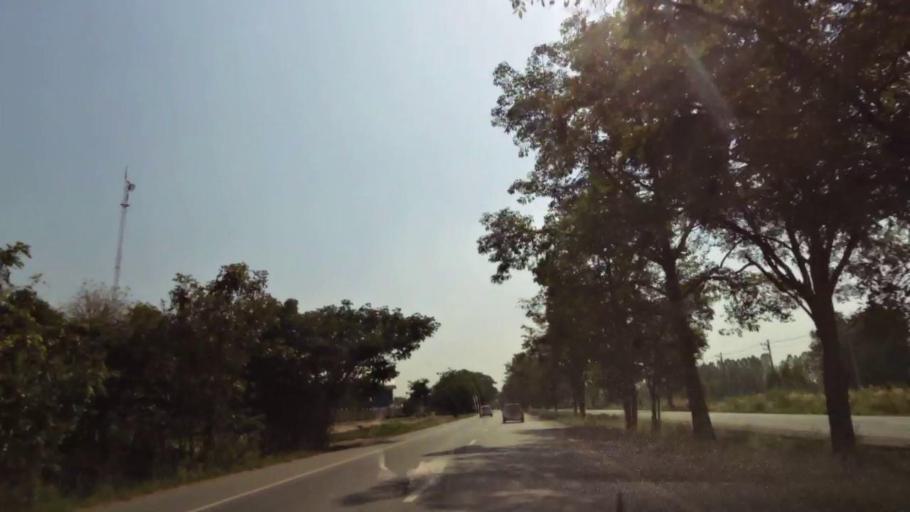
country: TH
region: Phichit
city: Bueng Na Rang
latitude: 16.0191
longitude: 100.1145
